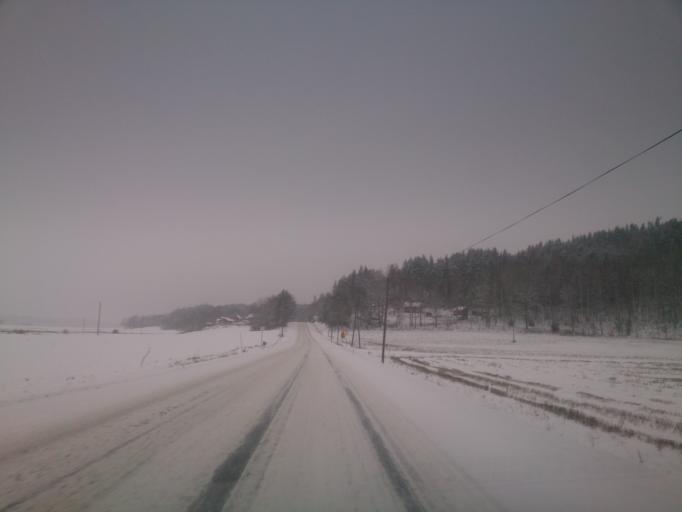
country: SE
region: OEstergoetland
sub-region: Norrkopings Kommun
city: Skarblacka
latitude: 58.6044
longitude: 15.8246
